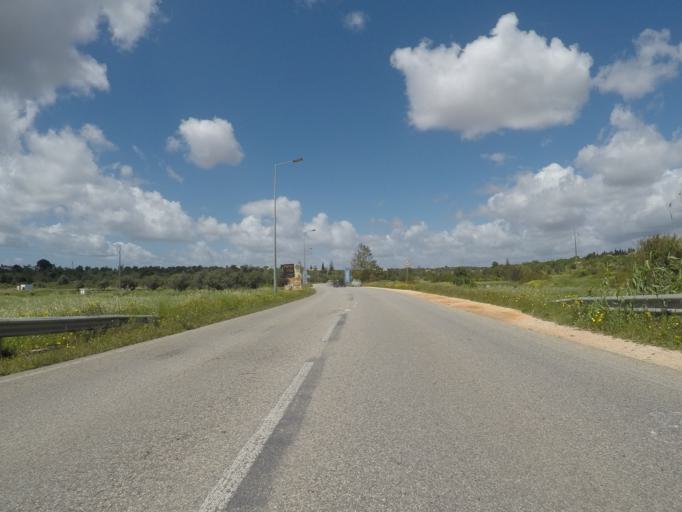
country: PT
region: Faro
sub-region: Silves
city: Armacao de Pera
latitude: 37.1161
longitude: -8.3452
